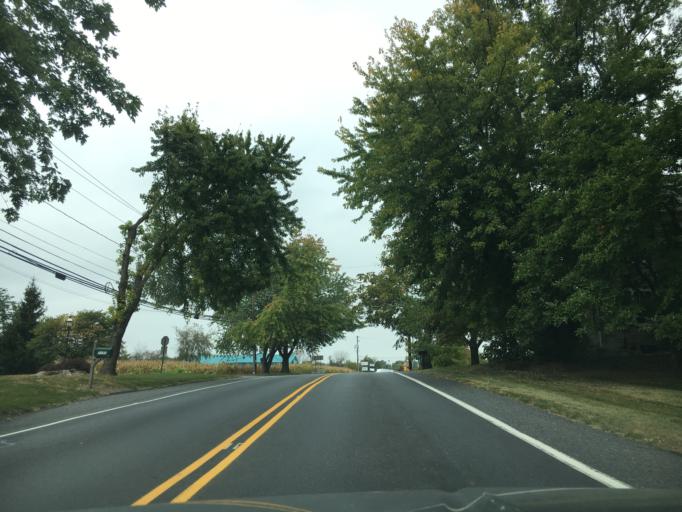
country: US
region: Pennsylvania
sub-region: Northampton County
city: Bath
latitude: 40.6973
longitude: -75.4167
